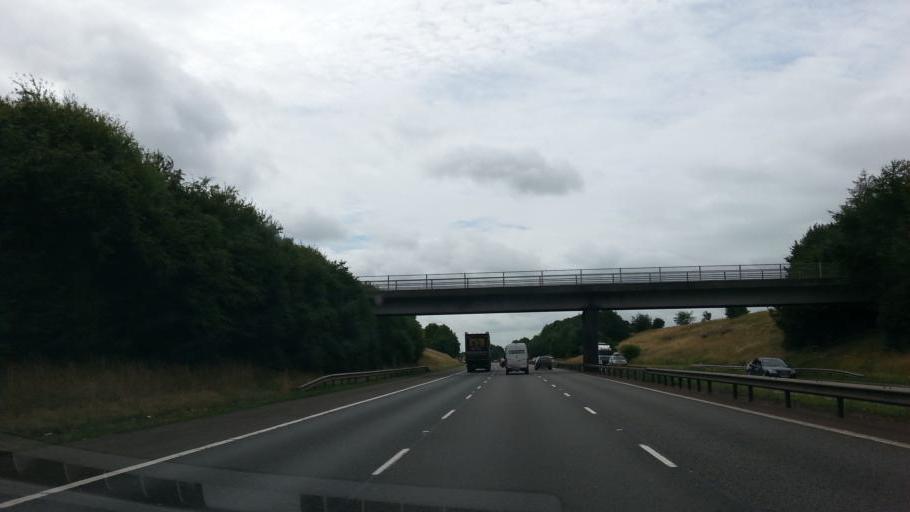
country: GB
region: England
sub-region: Oxfordshire
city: Adderbury
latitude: 52.0403
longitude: -1.3046
